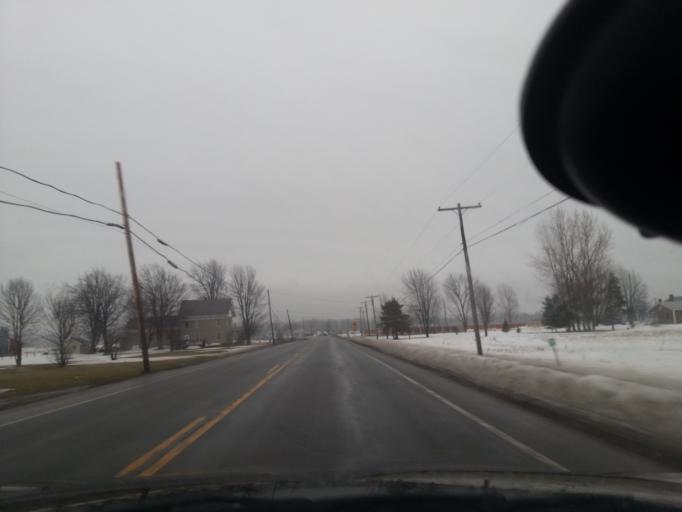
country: US
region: New York
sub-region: St. Lawrence County
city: Ogdensburg
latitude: 44.6660
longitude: -75.4679
